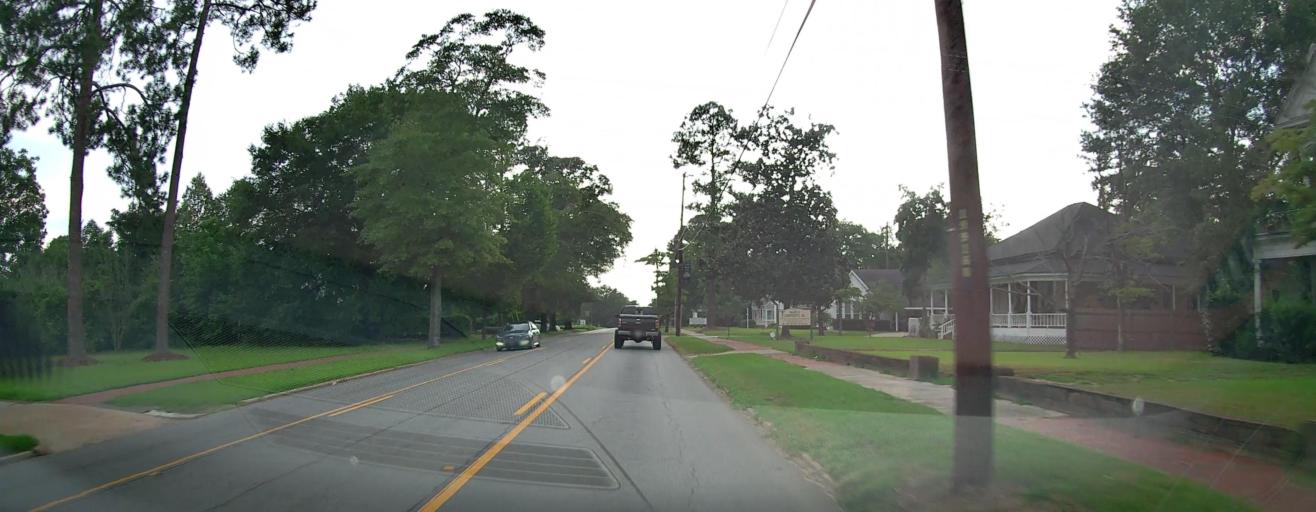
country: US
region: Georgia
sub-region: Laurens County
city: Dublin
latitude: 32.5369
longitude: -82.9185
